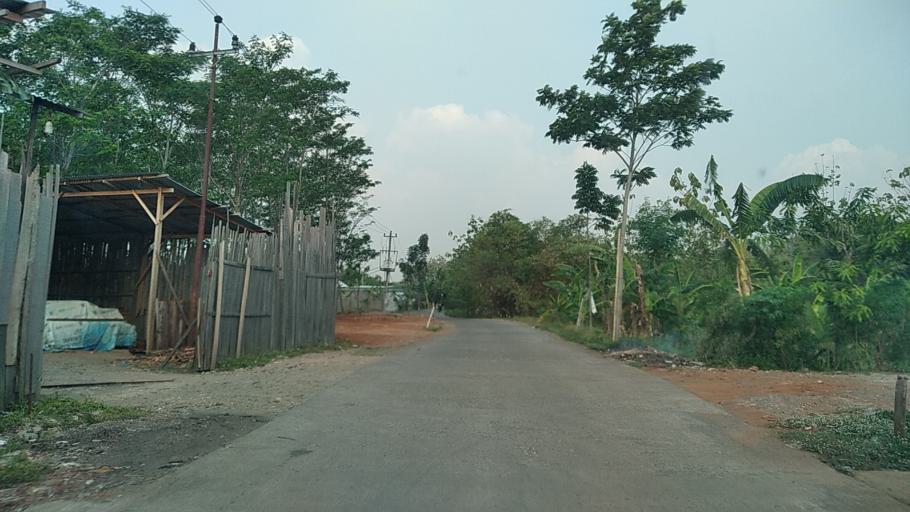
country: ID
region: Central Java
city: Mranggen
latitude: -7.0699
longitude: 110.4749
